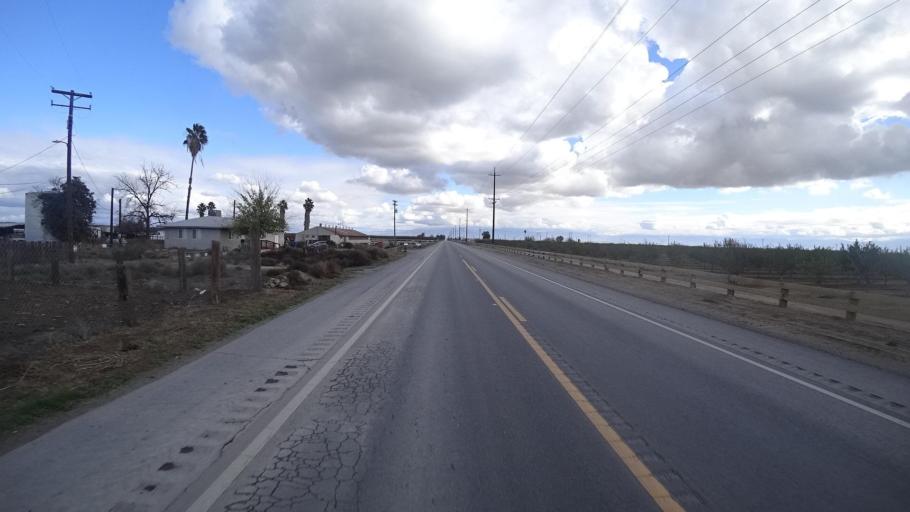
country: US
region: California
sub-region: Kern County
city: Greenfield
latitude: 35.2091
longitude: -119.0909
